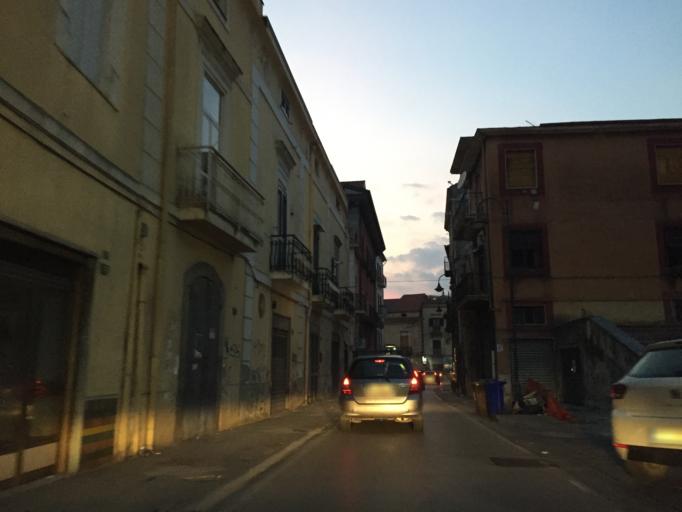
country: IT
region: Campania
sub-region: Provincia di Salerno
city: Nocera Inferiore
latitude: 40.7477
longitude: 14.6395
